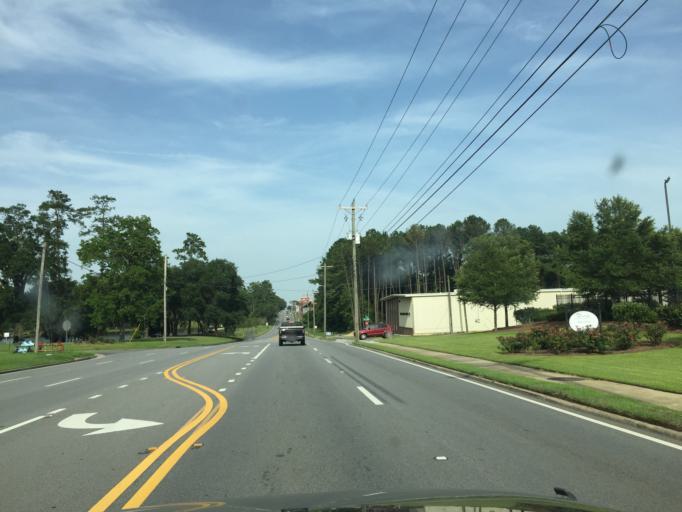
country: US
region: Georgia
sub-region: Thomas County
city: Thomasville
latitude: 30.8354
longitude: -83.9634
